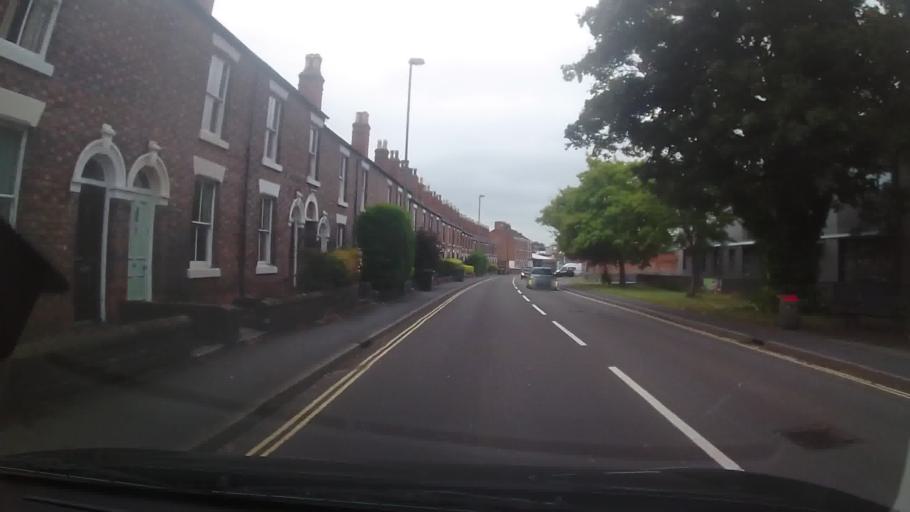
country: GB
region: England
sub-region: Shropshire
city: Shrewsbury
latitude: 52.7164
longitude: -2.7467
